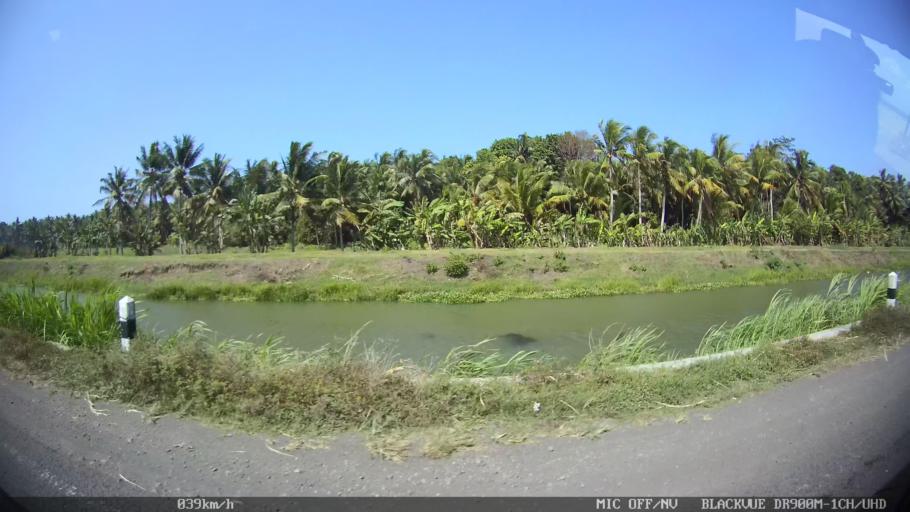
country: ID
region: Daerah Istimewa Yogyakarta
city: Srandakan
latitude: -7.9497
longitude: 110.1853
